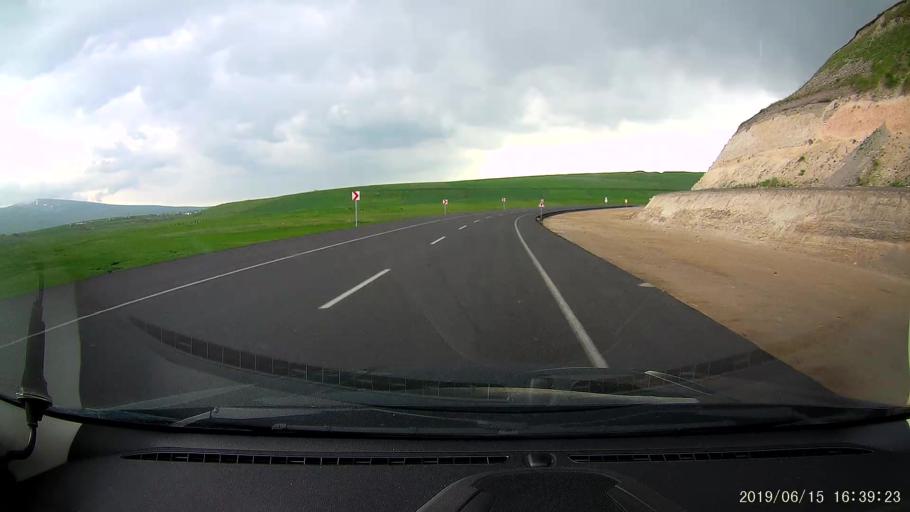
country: TR
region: Ardahan
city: Haskoy
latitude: 40.9833
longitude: 42.8971
